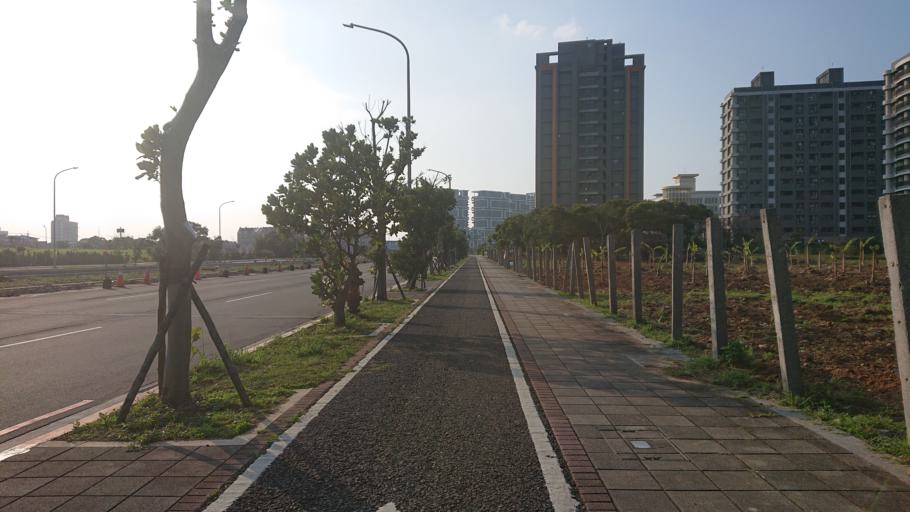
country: TW
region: Taipei
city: Taipei
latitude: 25.1909
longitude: 121.4295
